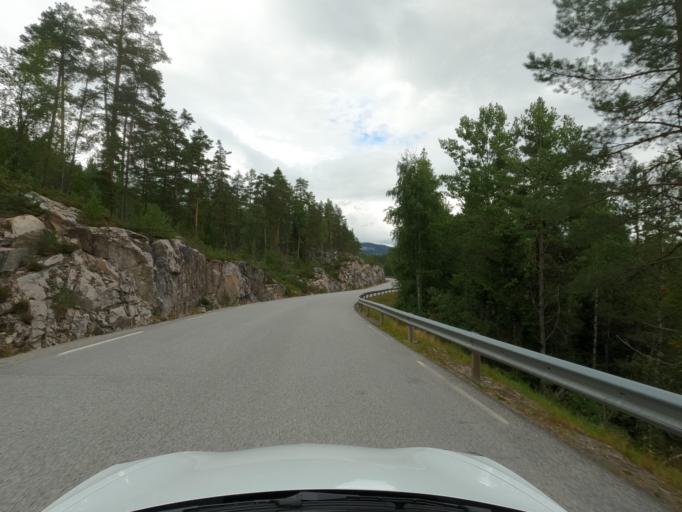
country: NO
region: Telemark
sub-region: Notodden
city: Notodden
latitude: 59.7023
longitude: 9.1503
